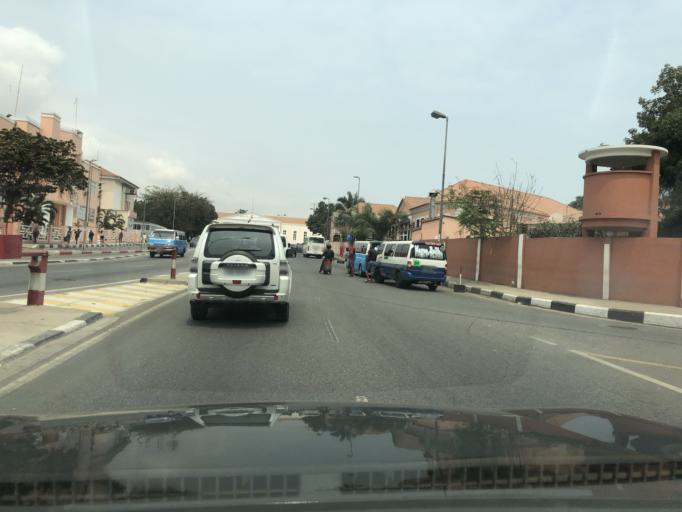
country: AO
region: Luanda
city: Luanda
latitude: -8.8218
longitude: 13.2274
